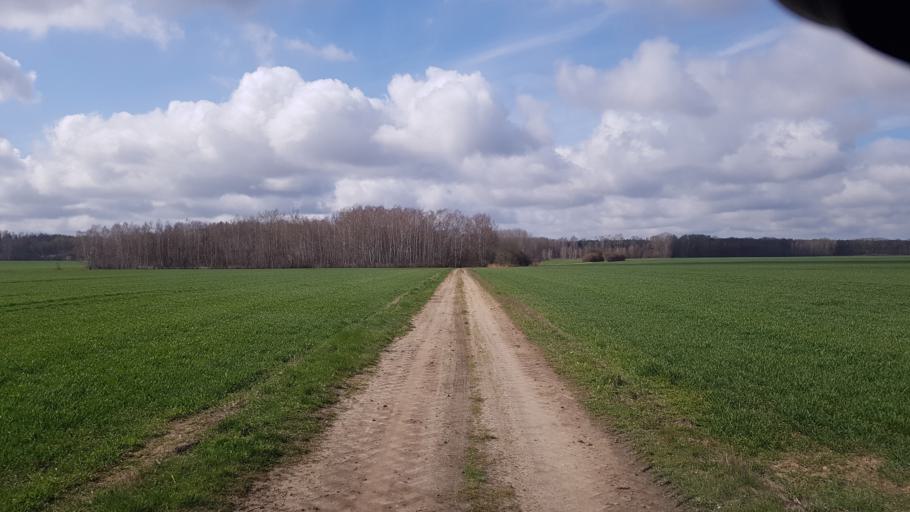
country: DE
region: Brandenburg
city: Doberlug-Kirchhain
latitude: 51.6490
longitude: 13.5350
